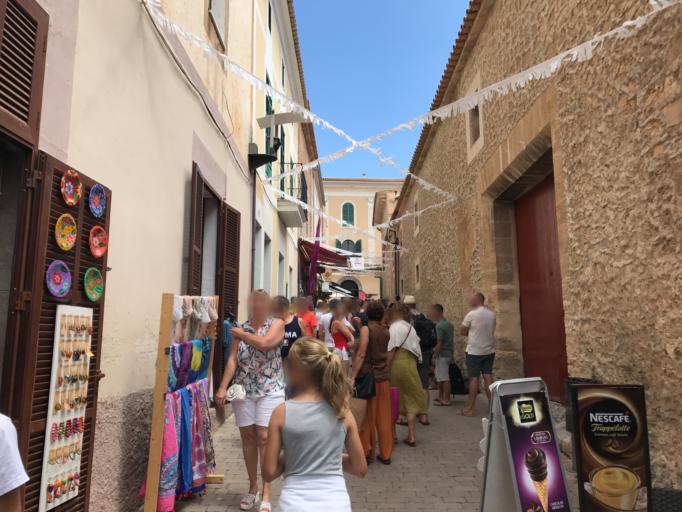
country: ES
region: Balearic Islands
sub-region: Illes Balears
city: Arta
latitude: 39.6941
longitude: 3.3508
